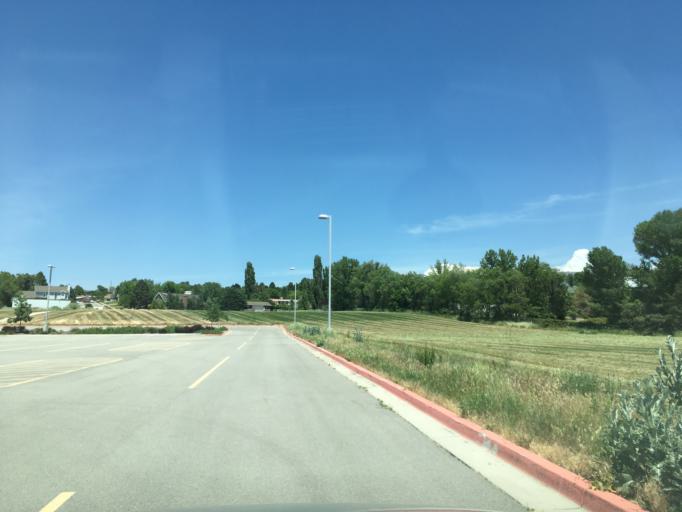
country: US
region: Utah
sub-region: Davis County
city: Hill Air Force Bace
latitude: 41.0978
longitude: -111.9796
